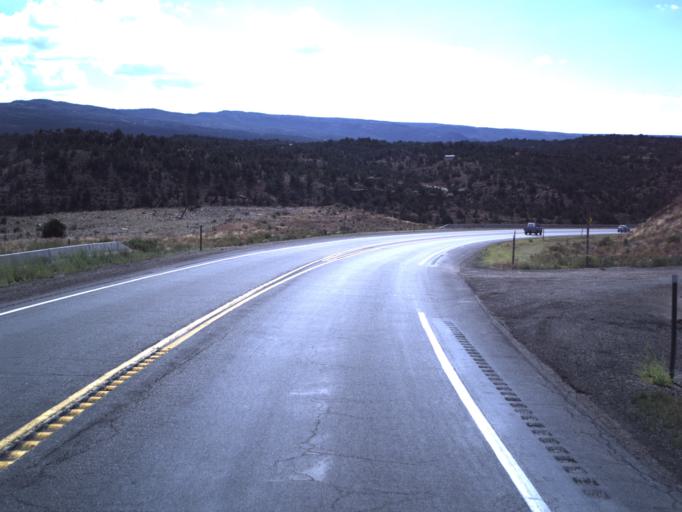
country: US
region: Utah
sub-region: Duchesne County
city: Duchesne
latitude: 40.1994
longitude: -110.7775
